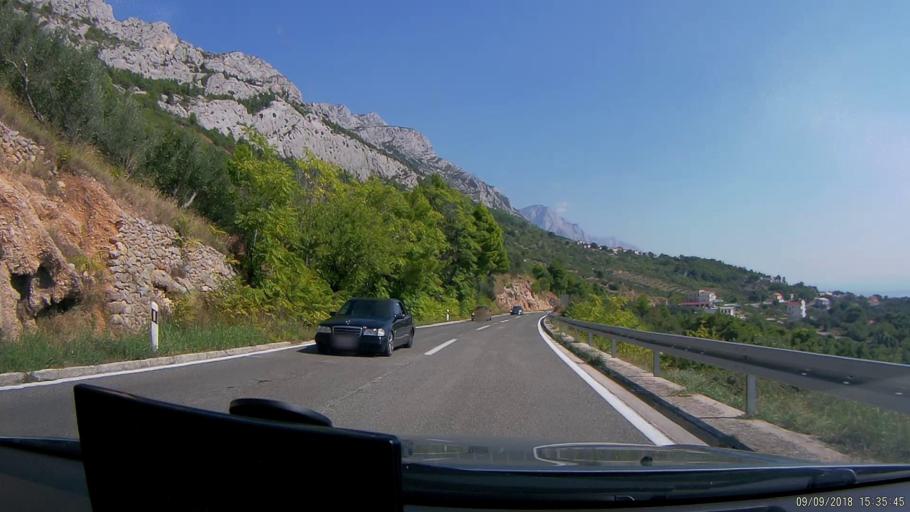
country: HR
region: Splitsko-Dalmatinska
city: Donja Brela
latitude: 43.3827
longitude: 16.9186
